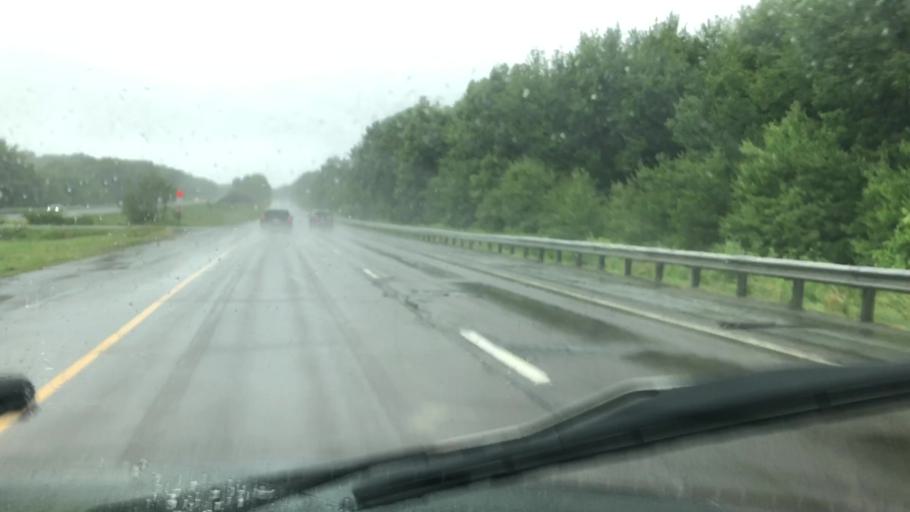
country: US
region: Pennsylvania
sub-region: Pike County
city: Gold Key Lake
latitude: 41.3441
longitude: -74.9226
